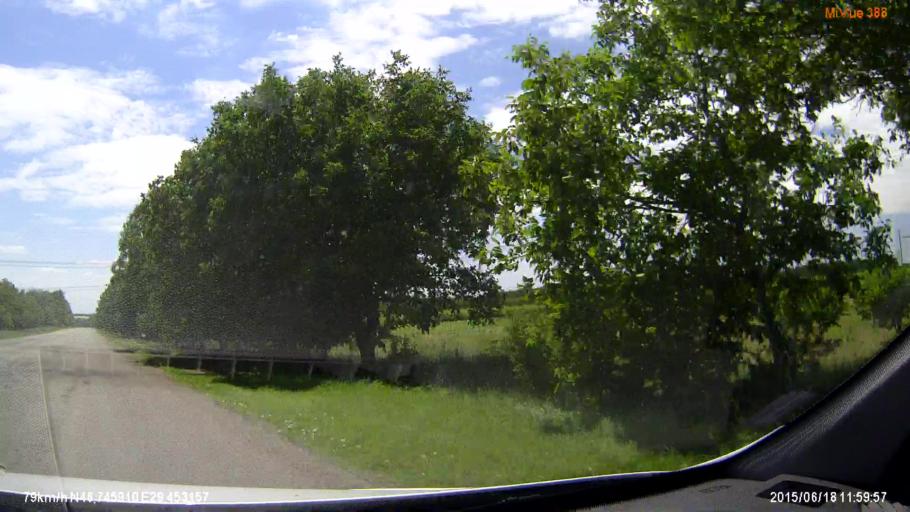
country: MD
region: Bender
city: Bender
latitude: 46.7463
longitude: 29.4533
